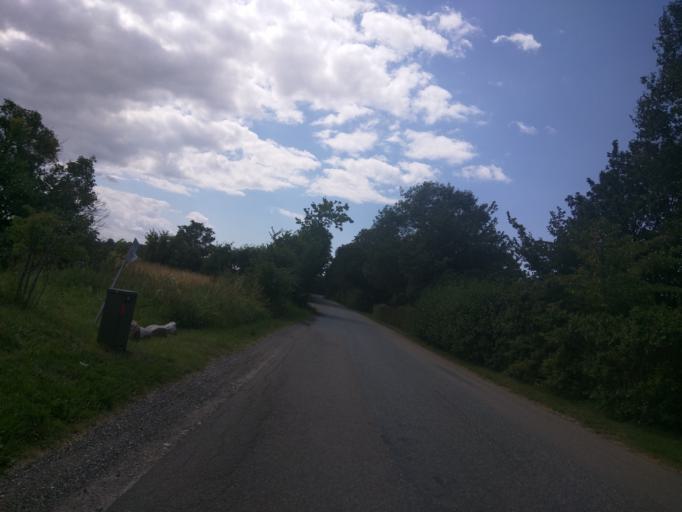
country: DK
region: Zealand
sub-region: Kalundborg Kommune
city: Svebolle
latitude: 55.6906
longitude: 11.2685
